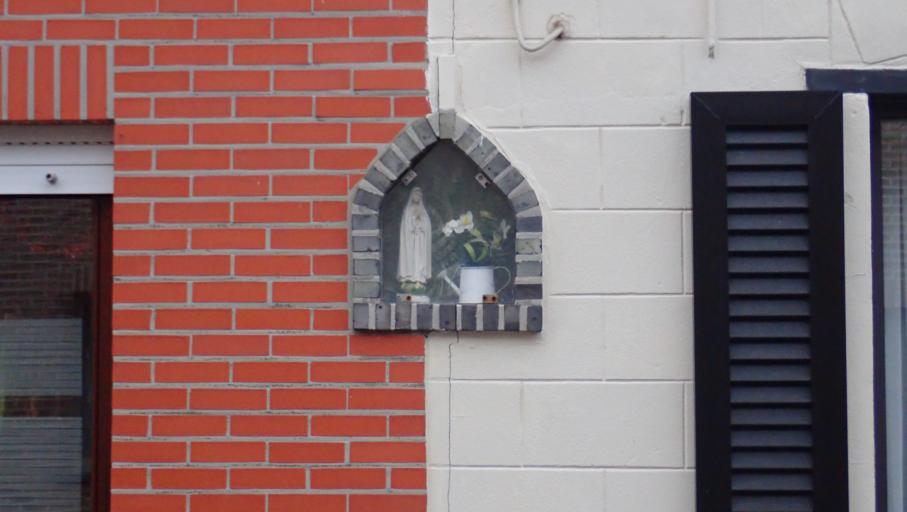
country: BE
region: Flanders
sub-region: Provincie Vlaams-Brabant
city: Opwijk
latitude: 50.9683
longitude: 4.1850
